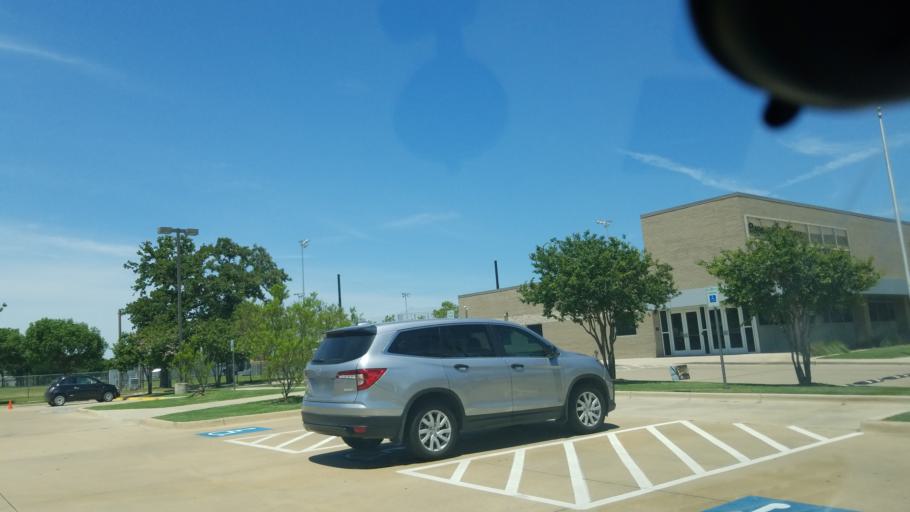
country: US
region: Texas
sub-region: Dallas County
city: Irving
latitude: 32.8215
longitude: -96.9465
